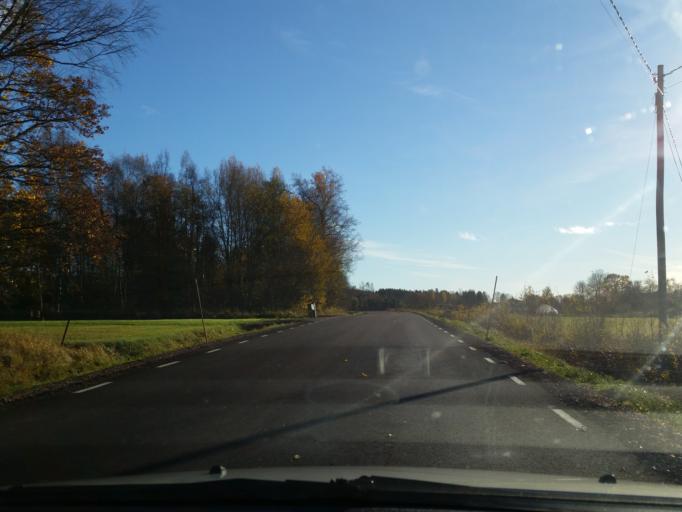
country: AX
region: Alands landsbygd
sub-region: Jomala
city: Jomala
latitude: 60.1894
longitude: 19.9606
